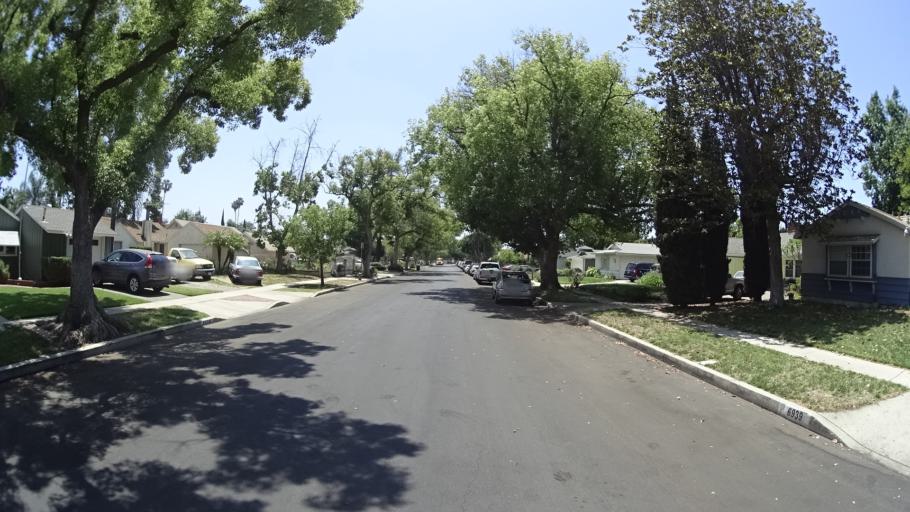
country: US
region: California
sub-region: Los Angeles County
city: Van Nuys
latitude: 34.1970
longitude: -118.4389
